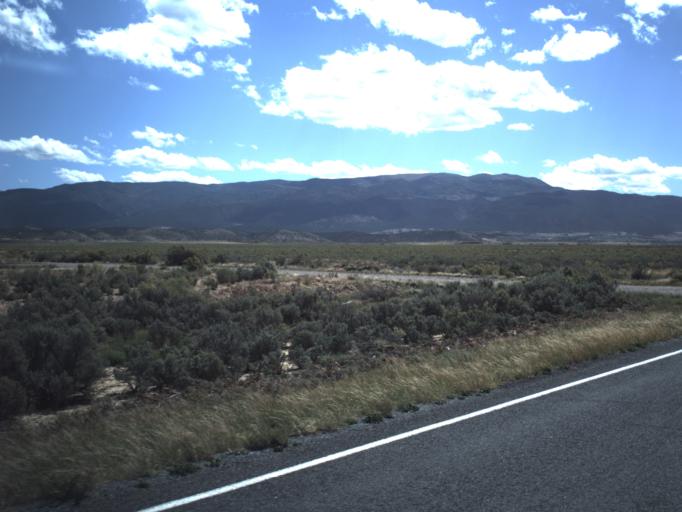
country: US
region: Utah
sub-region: Iron County
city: Enoch
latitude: 37.8286
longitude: -113.0504
